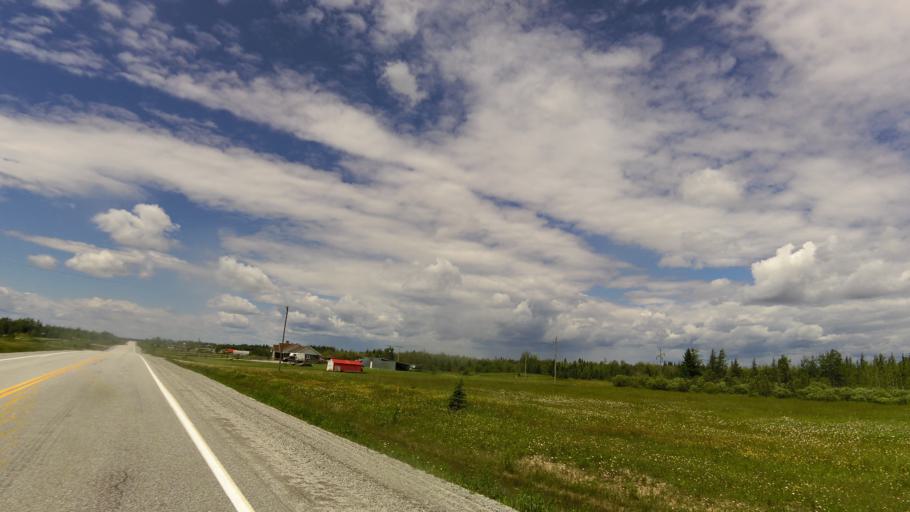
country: CA
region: Ontario
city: Kapuskasing
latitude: 49.3025
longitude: -81.9914
